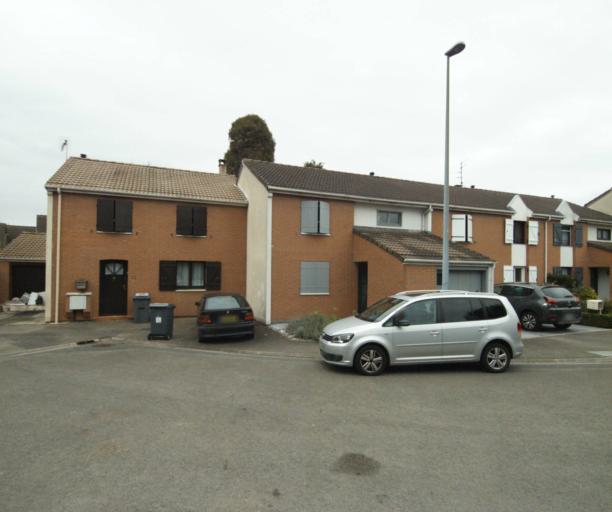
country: FR
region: Nord-Pas-de-Calais
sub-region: Departement du Nord
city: Lambersart
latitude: 50.6484
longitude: 3.0188
